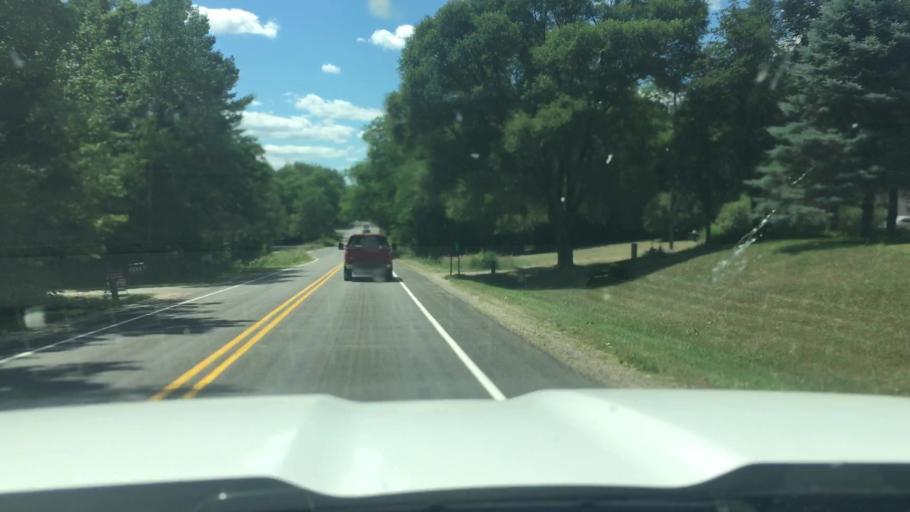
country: US
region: Michigan
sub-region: Kent County
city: Cedar Springs
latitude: 43.1755
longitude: -85.5982
